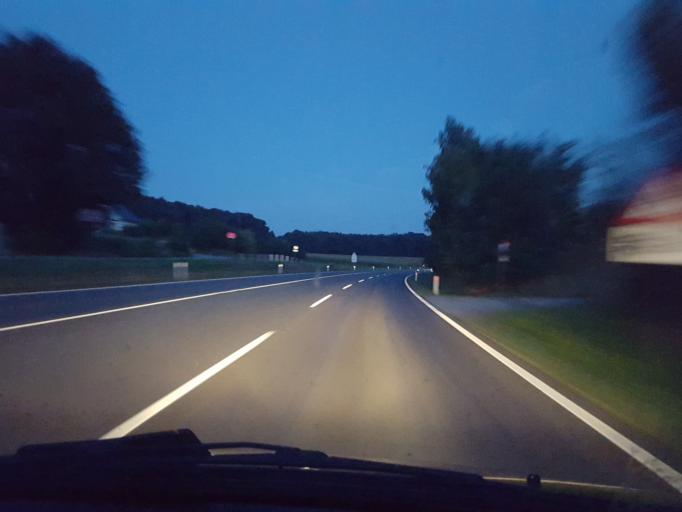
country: AT
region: Lower Austria
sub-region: Politischer Bezirk Scheibbs
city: Wieselburg
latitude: 48.1558
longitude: 15.1155
